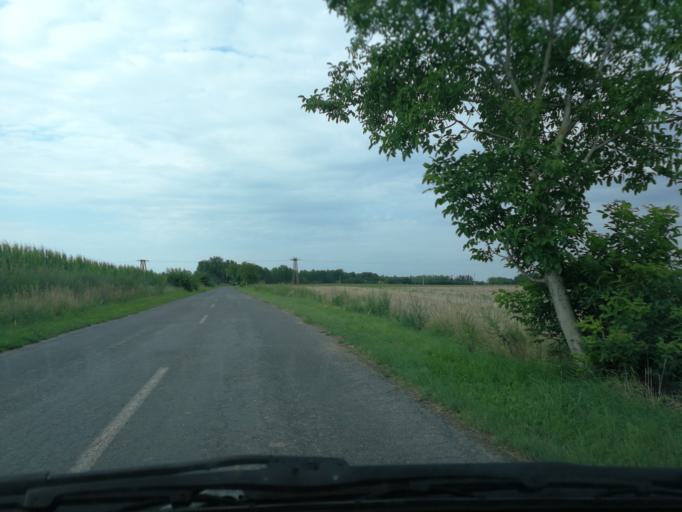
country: HU
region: Bacs-Kiskun
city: Kalocsa
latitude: 46.4559
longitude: 19.0334
